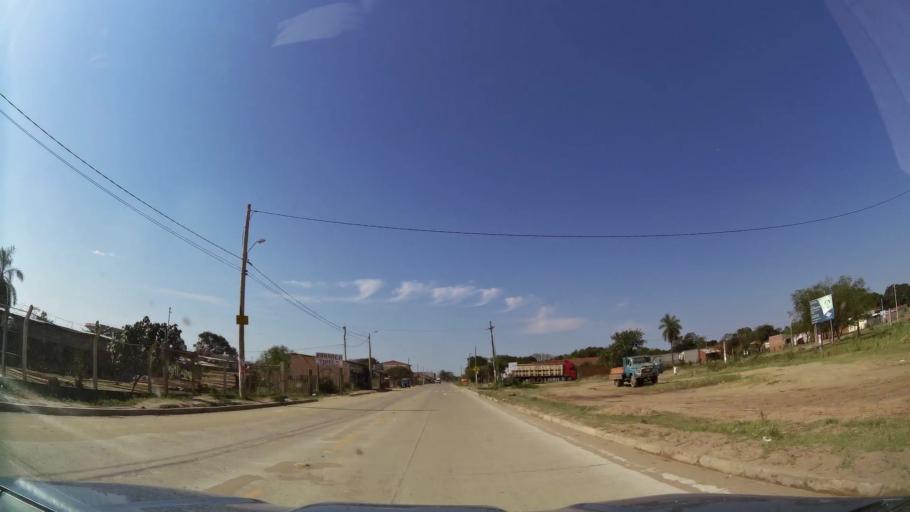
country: BO
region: Santa Cruz
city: Cotoca
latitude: -17.7264
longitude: -63.0866
